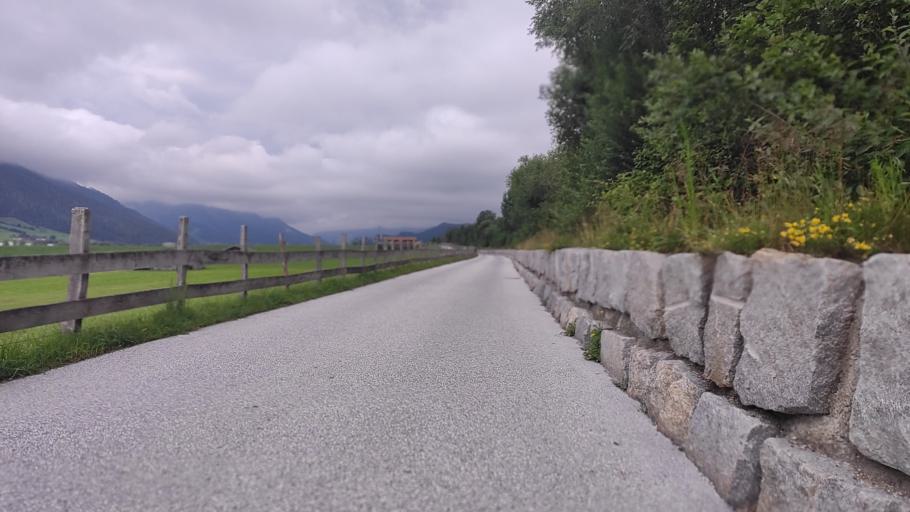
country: AT
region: Salzburg
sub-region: Politischer Bezirk Zell am See
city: Mittersill
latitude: 47.2838
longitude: 12.4685
